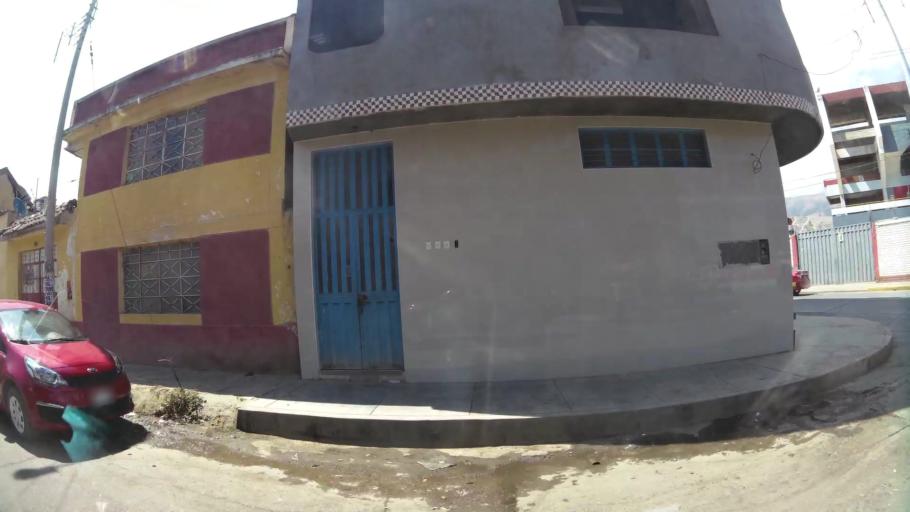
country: PE
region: Junin
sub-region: Provincia de Huancayo
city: Huancayo
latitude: -12.0719
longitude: -75.2027
